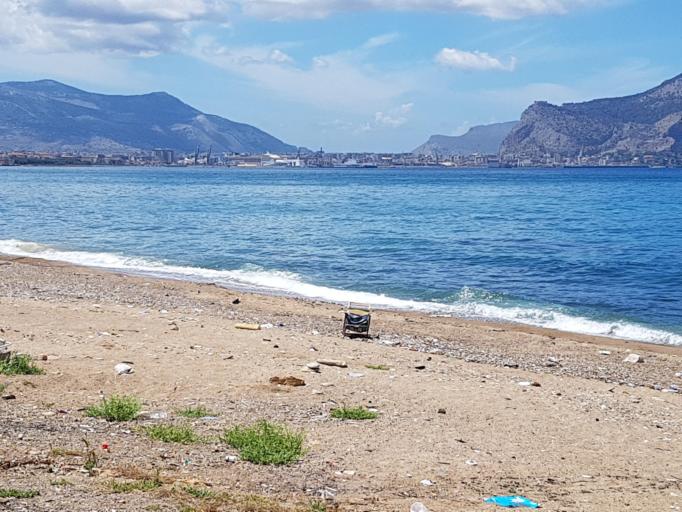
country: IT
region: Sicily
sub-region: Palermo
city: Ciaculli
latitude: 38.0972
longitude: 13.4111
